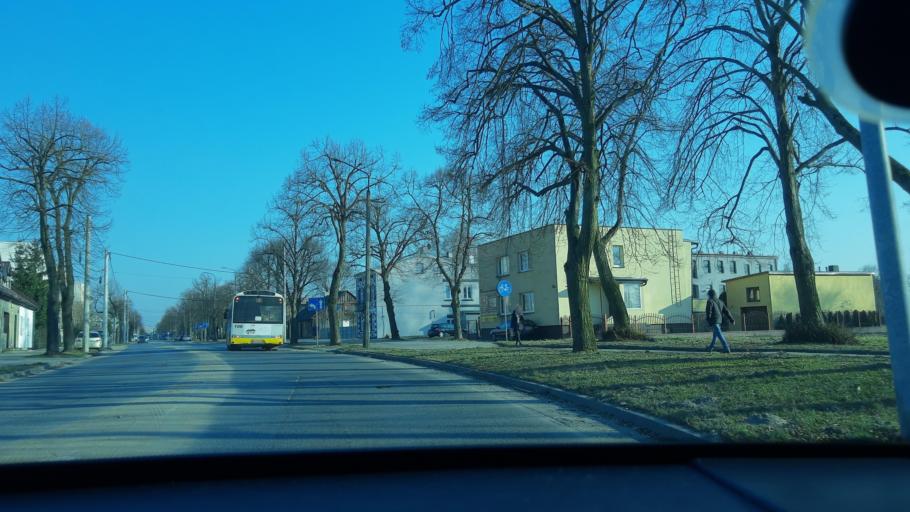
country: PL
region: Lodz Voivodeship
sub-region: Powiat zdunskowolski
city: Zdunska Wola
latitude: 51.6067
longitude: 18.9215
